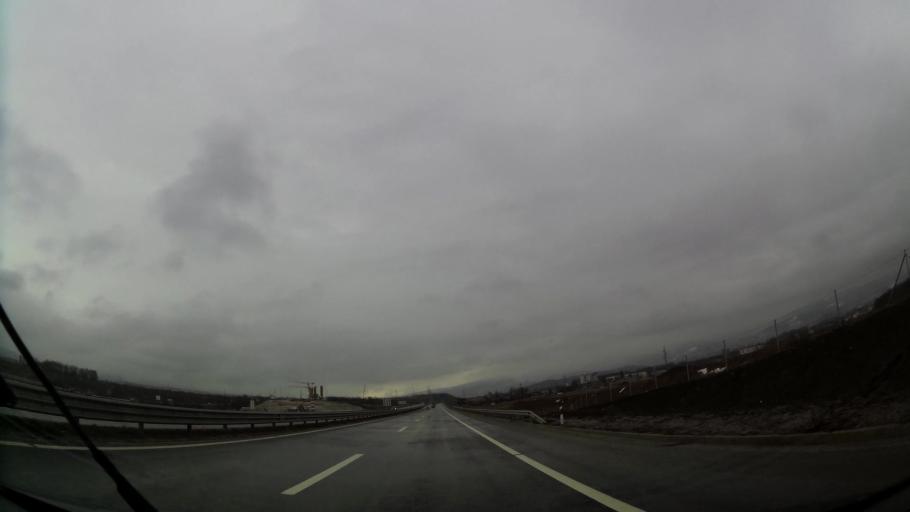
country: XK
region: Ferizaj
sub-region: Komuna e Kacanikut
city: Kacanik
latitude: 42.2833
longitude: 21.2091
